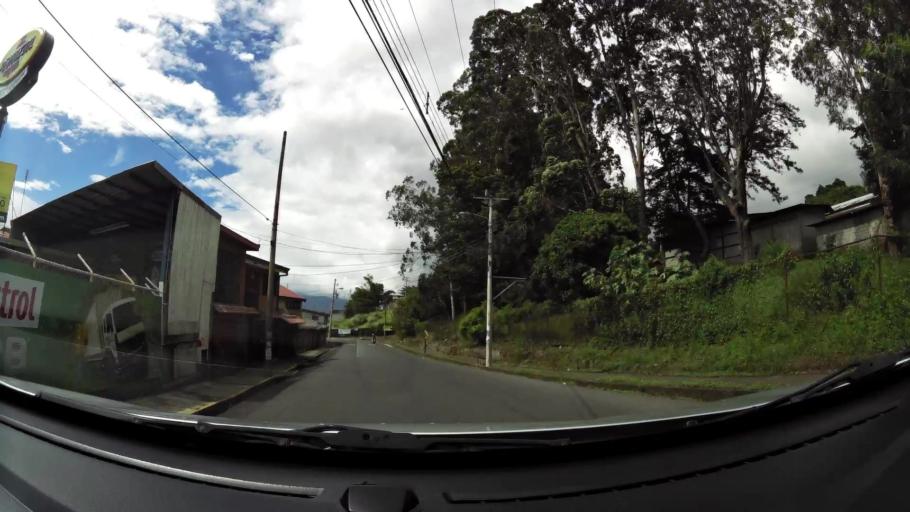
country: CR
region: Cartago
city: Tres Rios
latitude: 9.9096
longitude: -83.9883
